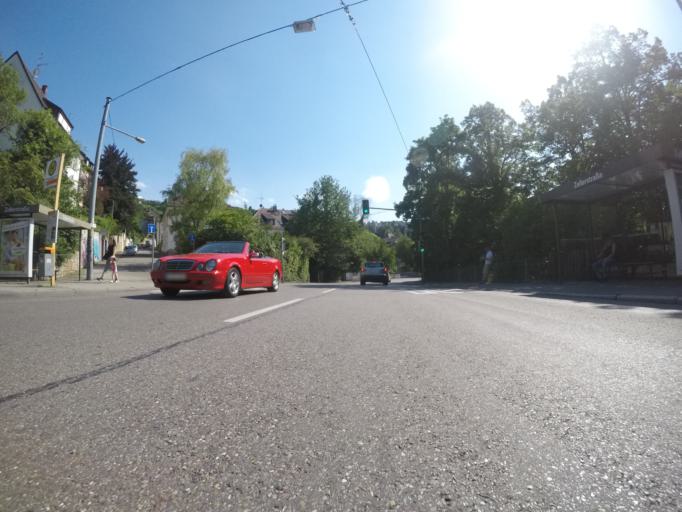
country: DE
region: Baden-Wuerttemberg
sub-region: Regierungsbezirk Stuttgart
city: Stuttgart
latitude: 48.7625
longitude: 9.1778
